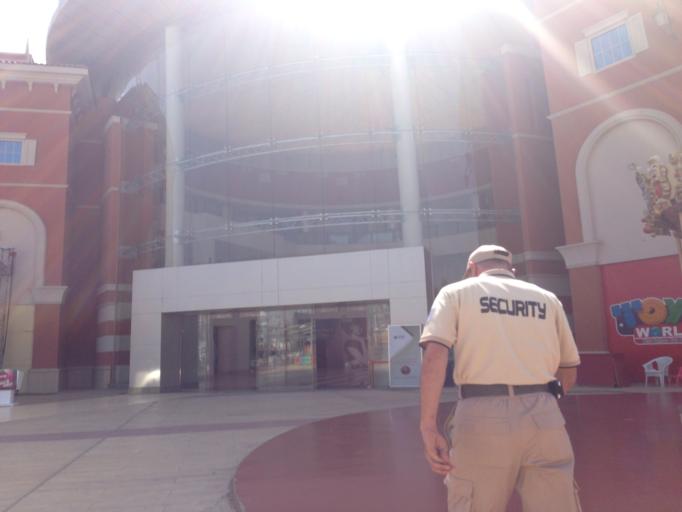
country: EG
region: Muhafazat al Qalyubiyah
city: Al Khankah
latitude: 30.0647
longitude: 31.4235
